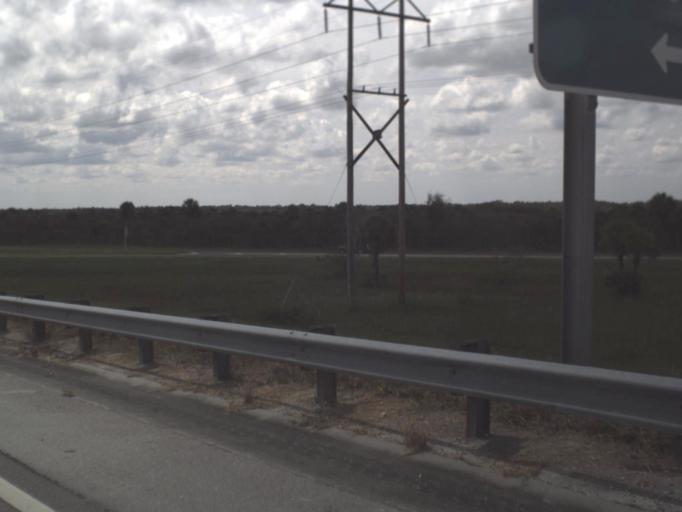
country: US
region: Florida
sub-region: Collier County
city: Immokalee
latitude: 26.1529
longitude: -81.3451
